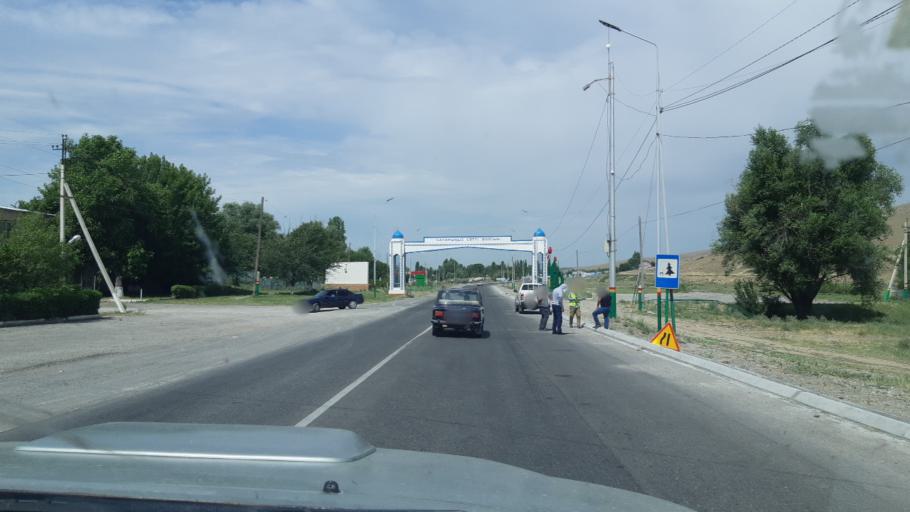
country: KZ
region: Ongtustik Qazaqstan
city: Turar Ryskulov
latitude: 42.5491
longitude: 70.3063
